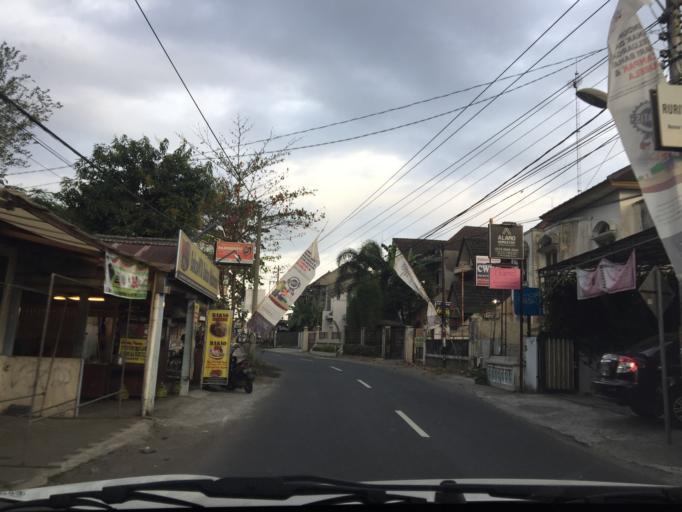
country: ID
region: Daerah Istimewa Yogyakarta
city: Melati
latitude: -7.7342
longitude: 110.3921
